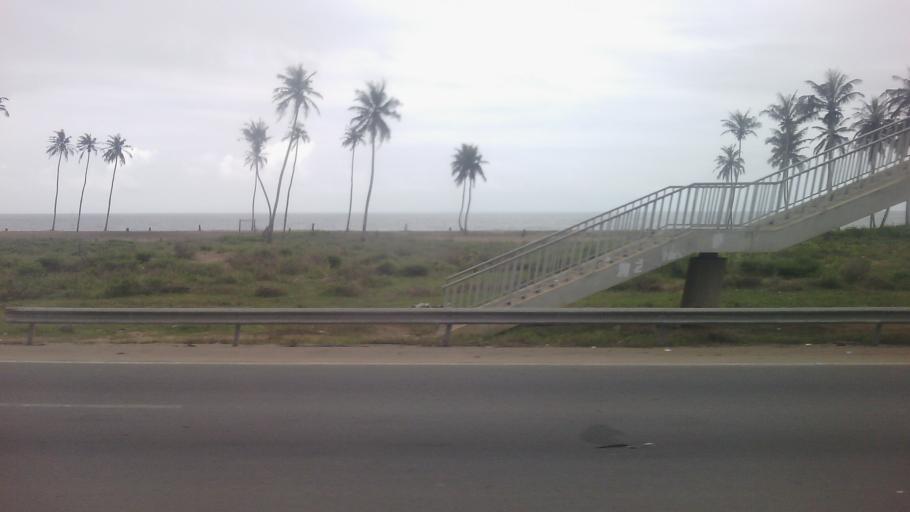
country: CI
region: Lagunes
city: Bingerville
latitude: 5.2373
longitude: -3.8827
